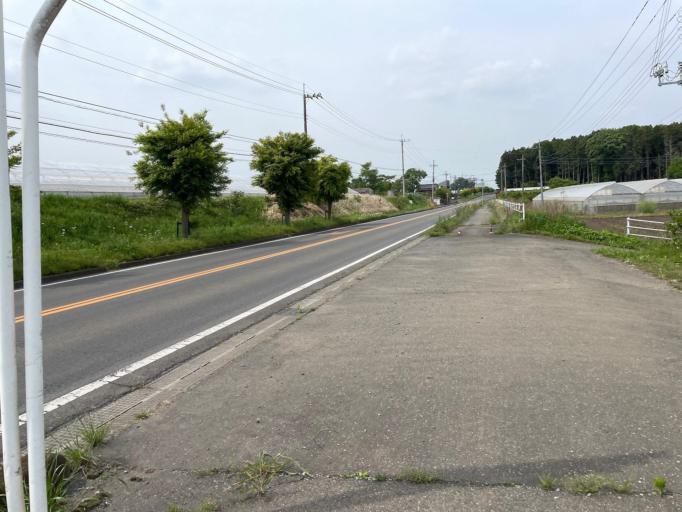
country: JP
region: Tochigi
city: Mibu
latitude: 36.3804
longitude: 139.8044
